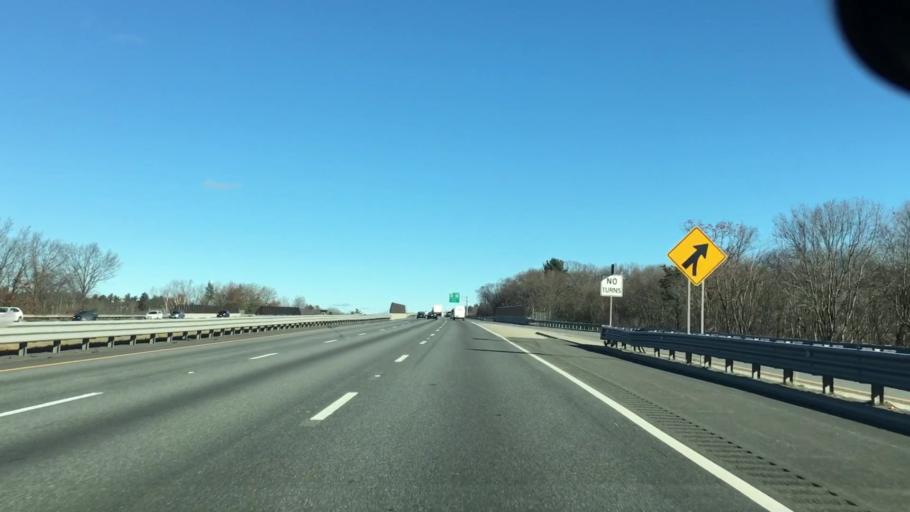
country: US
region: Massachusetts
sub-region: Middlesex County
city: Littleton Common
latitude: 42.5232
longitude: -71.5059
